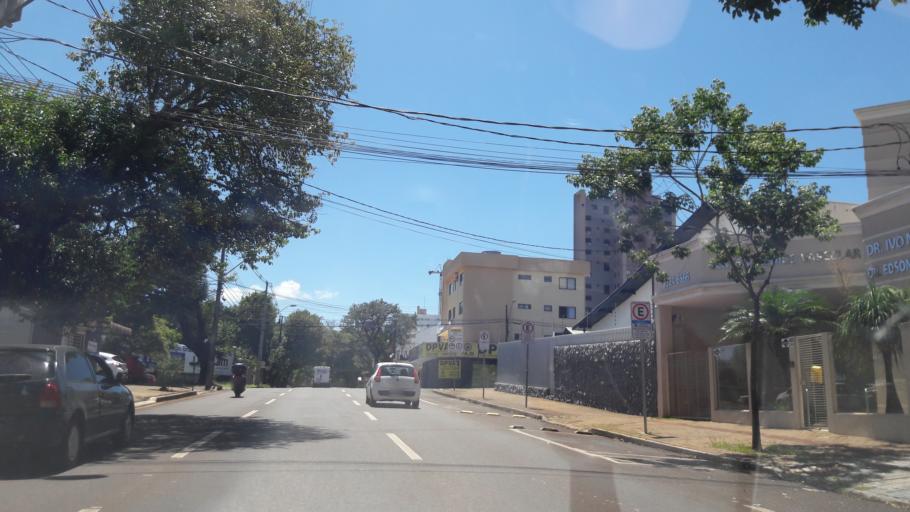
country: BR
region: Parana
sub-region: Cascavel
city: Cascavel
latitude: -24.9519
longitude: -53.4634
